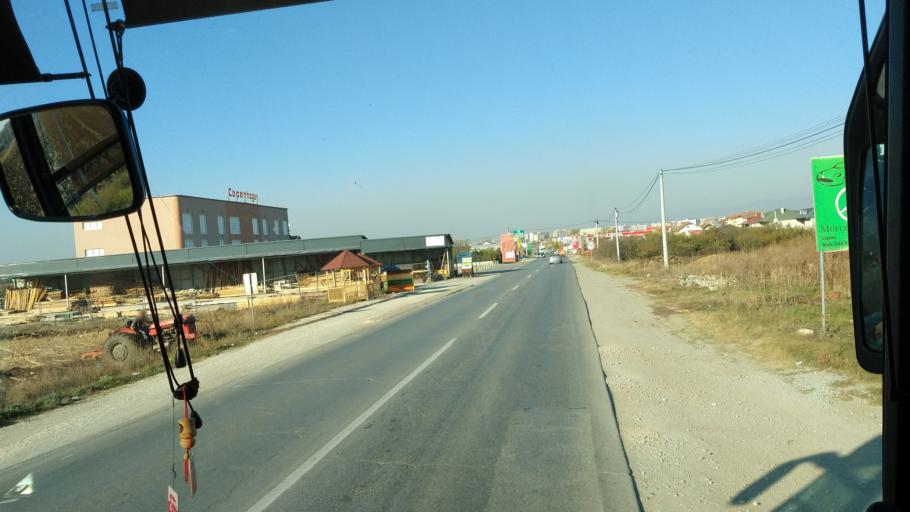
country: XK
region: Pristina
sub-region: Lipjan
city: Lipljan
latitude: 42.5045
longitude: 21.1103
